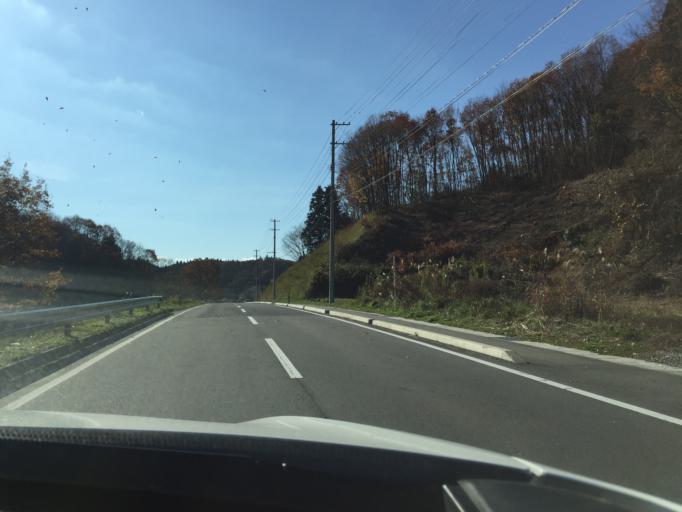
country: JP
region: Fukushima
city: Ishikawa
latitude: 37.2240
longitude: 140.5682
